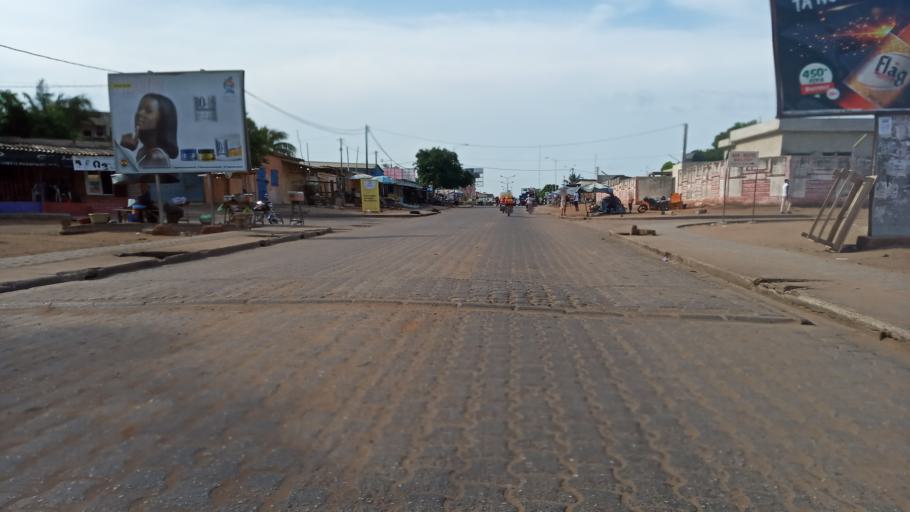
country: TG
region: Maritime
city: Lome
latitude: 6.1608
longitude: 1.2662
